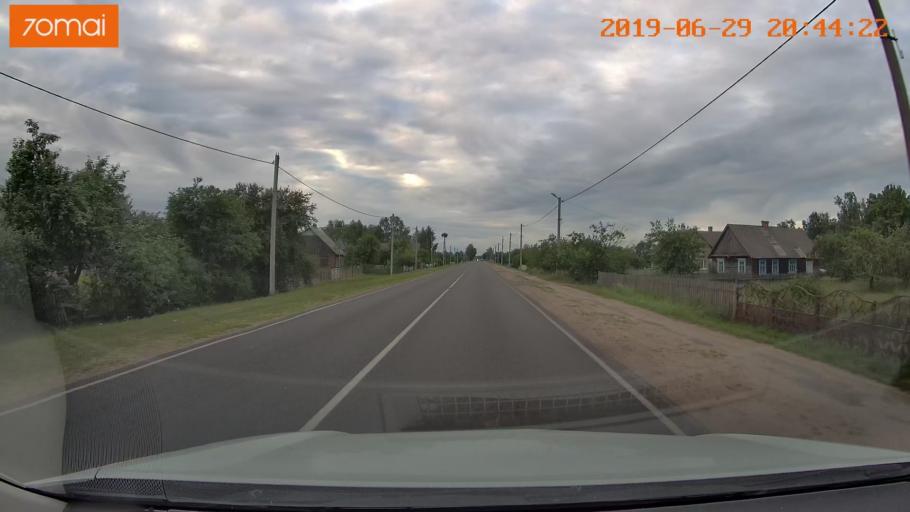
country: BY
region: Brest
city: Hantsavichy
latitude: 52.6129
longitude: 26.3073
